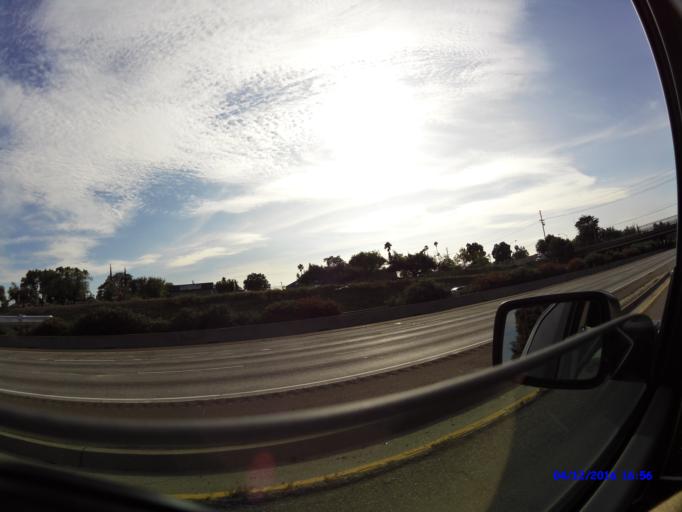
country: US
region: California
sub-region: Stanislaus County
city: Modesto
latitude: 37.6375
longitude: -121.0045
